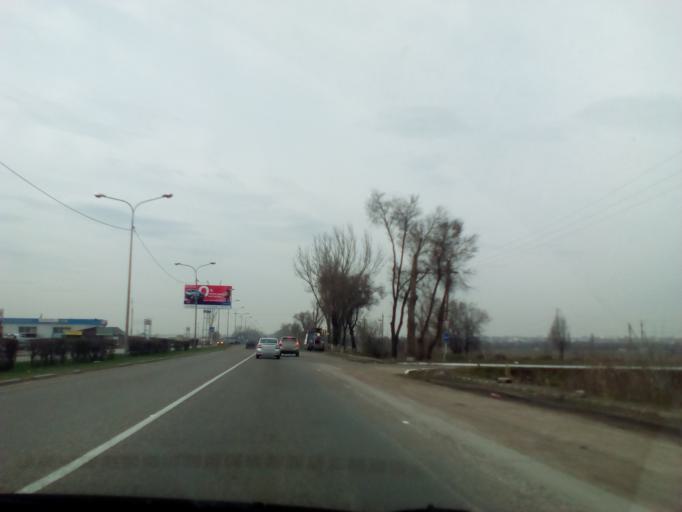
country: KZ
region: Almaty Oblysy
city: Burunday
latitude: 43.2207
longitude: 76.6304
